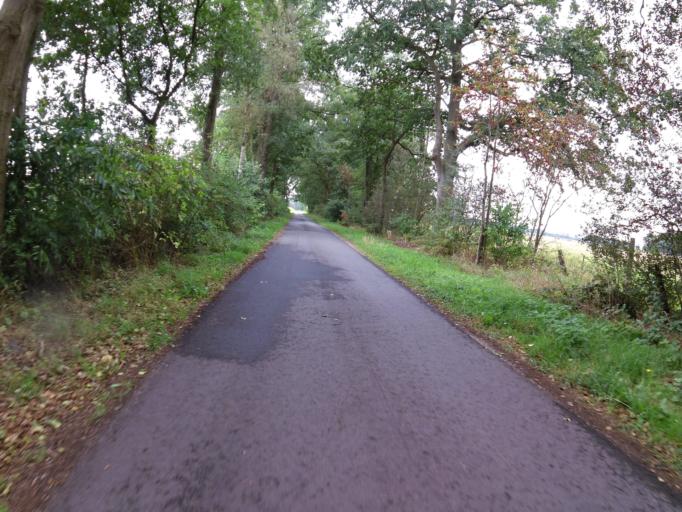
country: DE
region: Lower Saxony
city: Scheessel
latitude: 53.1584
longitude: 9.4556
